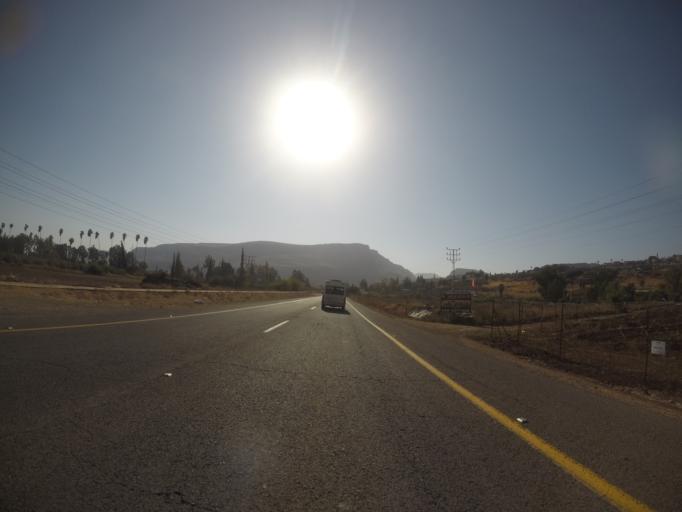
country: IL
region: Northern District
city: Tiberias
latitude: 32.8421
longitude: 35.5138
